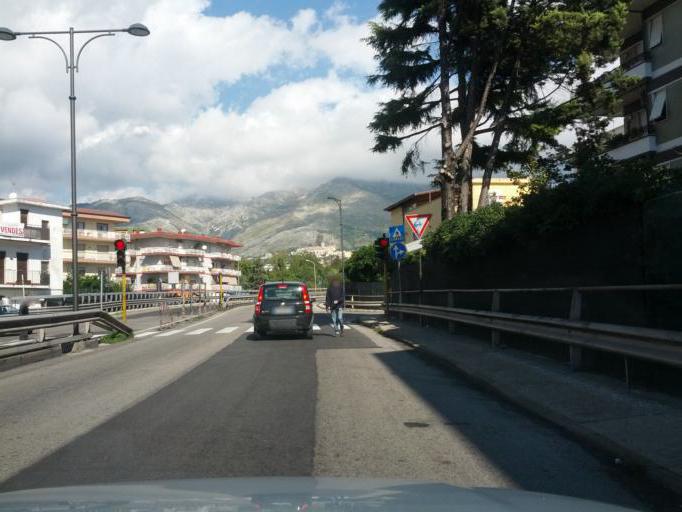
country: IT
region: Latium
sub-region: Provincia di Latina
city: Formia
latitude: 41.2632
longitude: 13.6207
